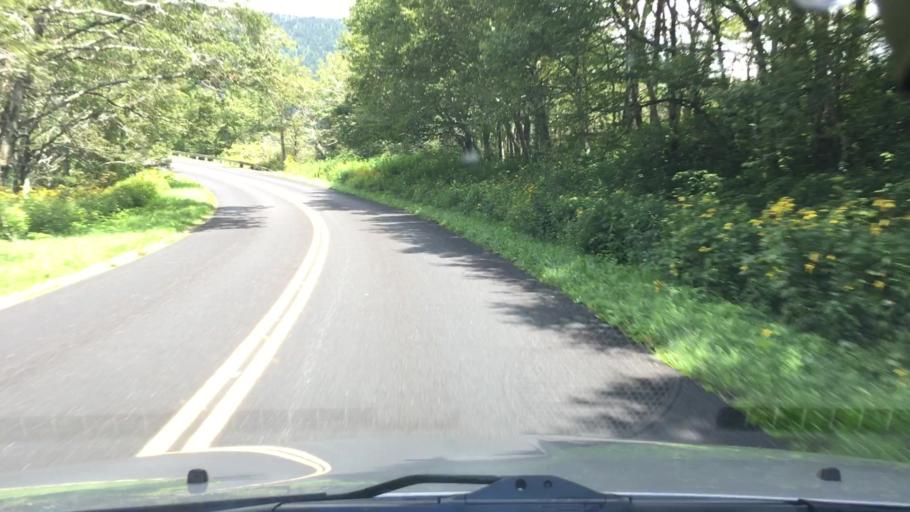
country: US
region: North Carolina
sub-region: Buncombe County
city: Black Mountain
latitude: 35.7316
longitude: -82.3461
